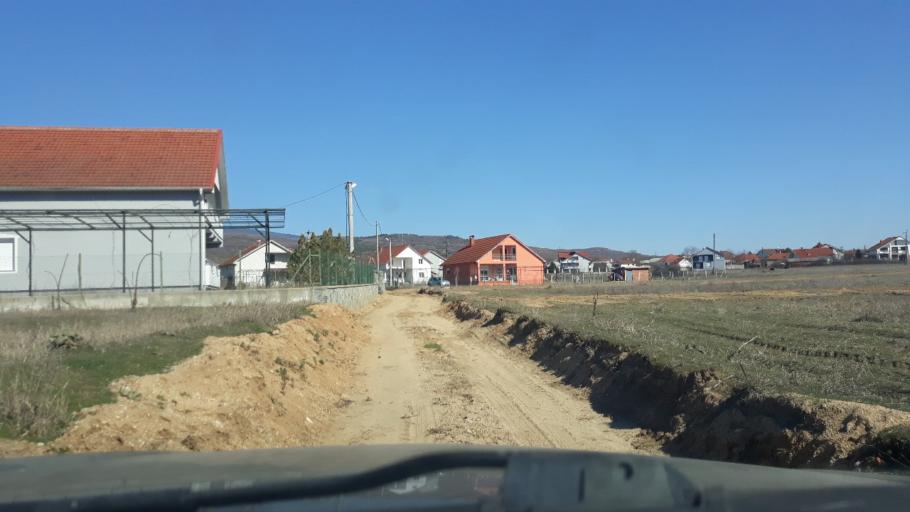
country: MK
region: Novo Selo
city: Novo Selo
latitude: 41.4143
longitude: 22.8700
